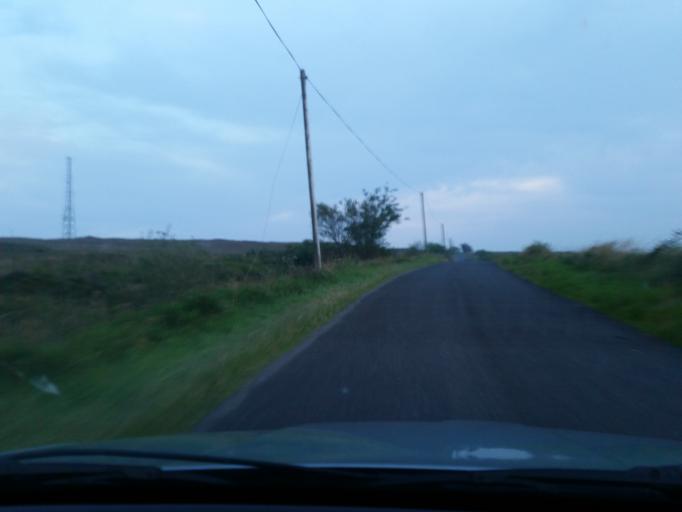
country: IE
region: Ulster
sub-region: County Monaghan
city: Clones
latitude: 54.2747
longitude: -7.2743
